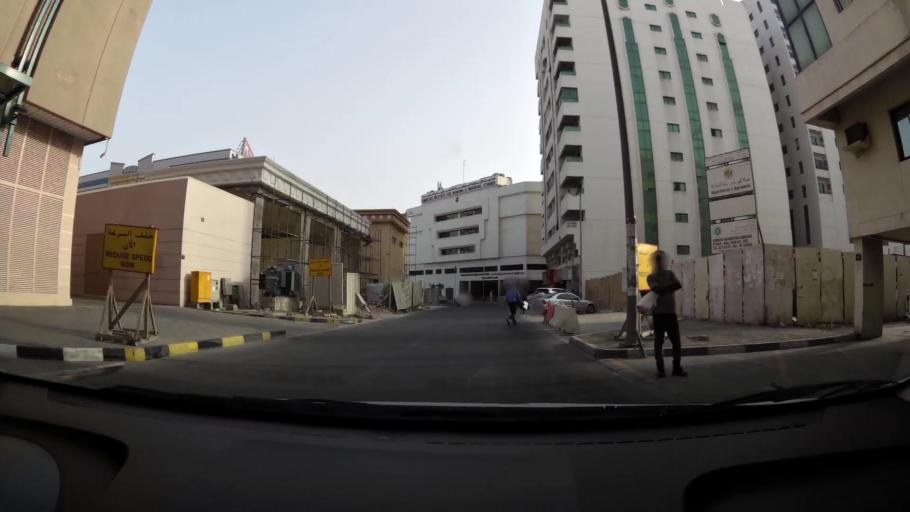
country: AE
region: Ash Shariqah
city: Sharjah
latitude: 25.3445
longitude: 55.3981
